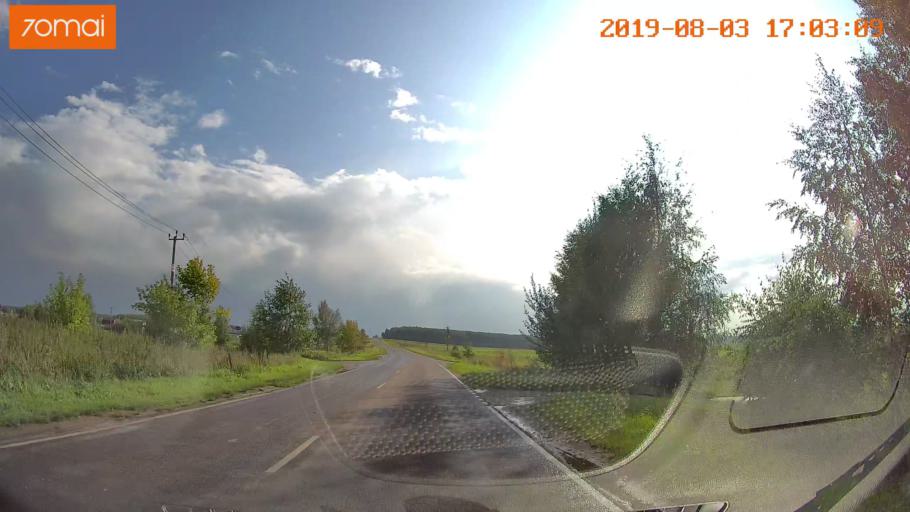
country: RU
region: Moskovskaya
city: Troitskoye
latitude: 55.3408
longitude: 38.5767
